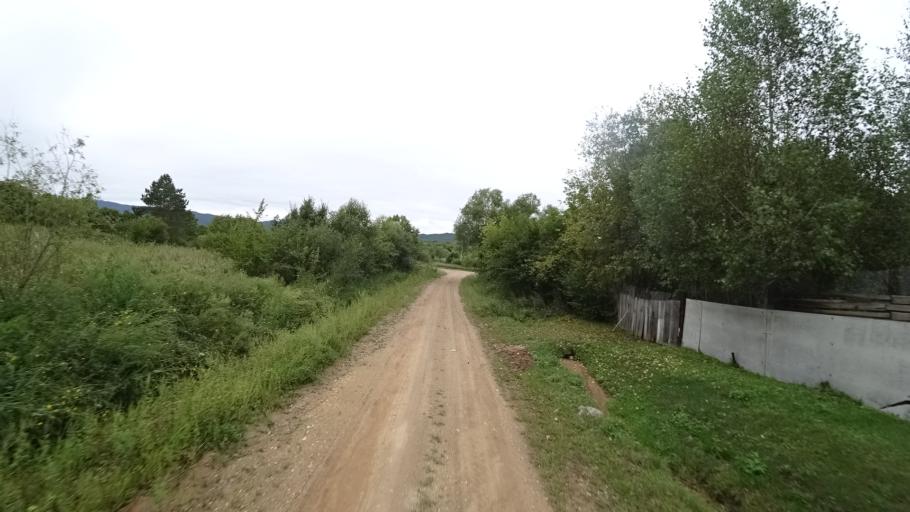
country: RU
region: Primorskiy
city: Rettikhovka
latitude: 44.1626
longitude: 132.7426
